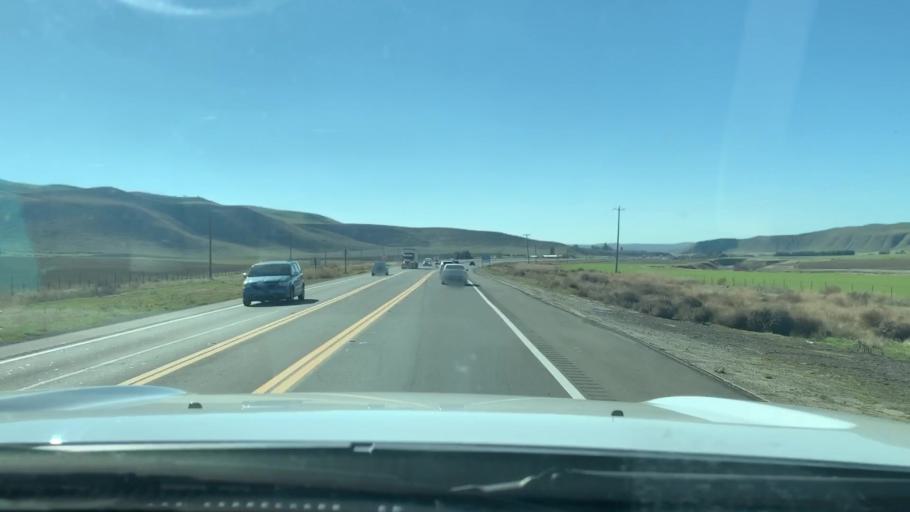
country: US
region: California
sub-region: San Luis Obispo County
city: Shandon
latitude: 35.6822
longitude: -120.3401
